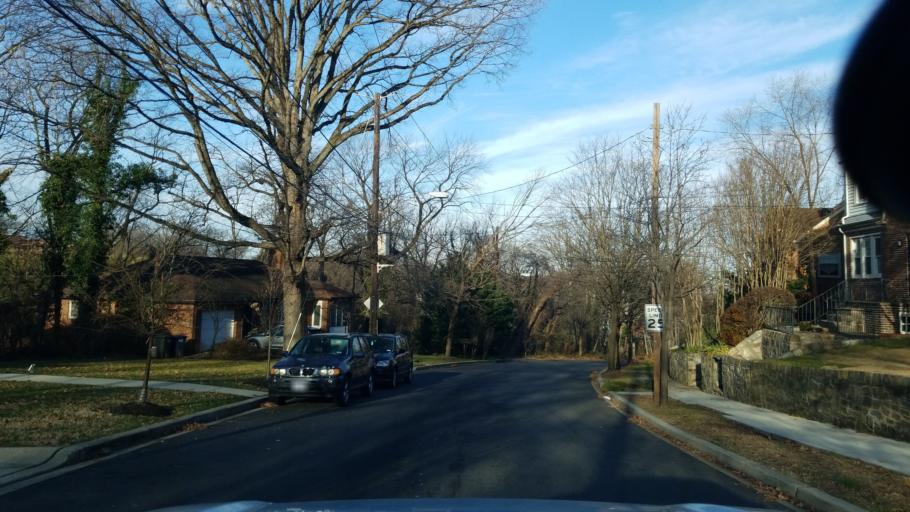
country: US
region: Maryland
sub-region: Prince George's County
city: Silver Hill
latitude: 38.8627
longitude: -76.9667
